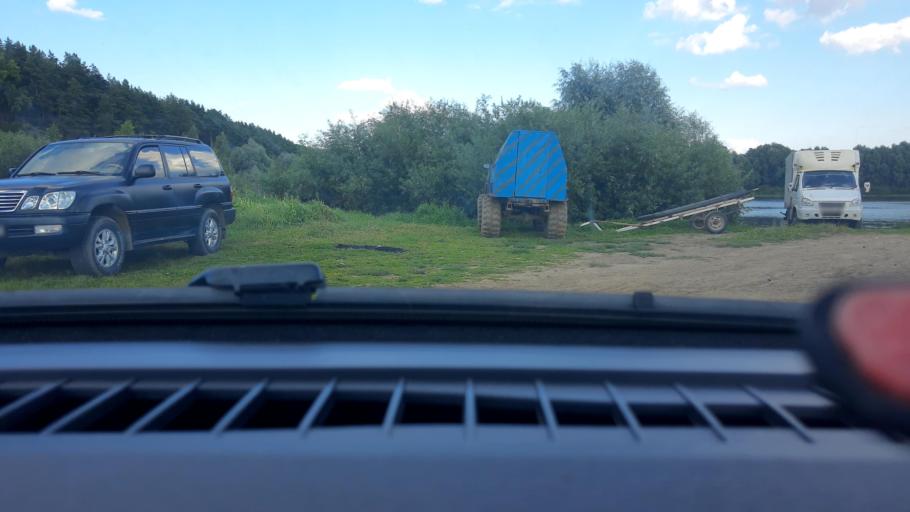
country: RU
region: Nizjnij Novgorod
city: Burevestnik
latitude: 56.1914
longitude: 43.7721
